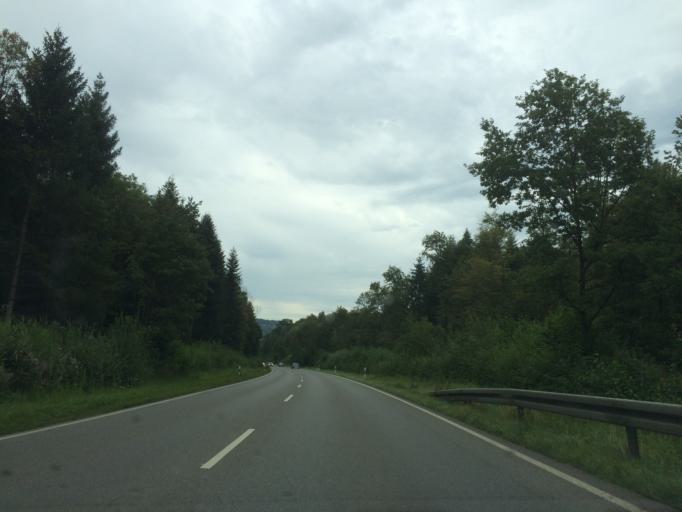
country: DE
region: Baden-Wuerttemberg
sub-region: Tuebingen Region
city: Ravensburg
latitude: 47.7689
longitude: 9.5780
